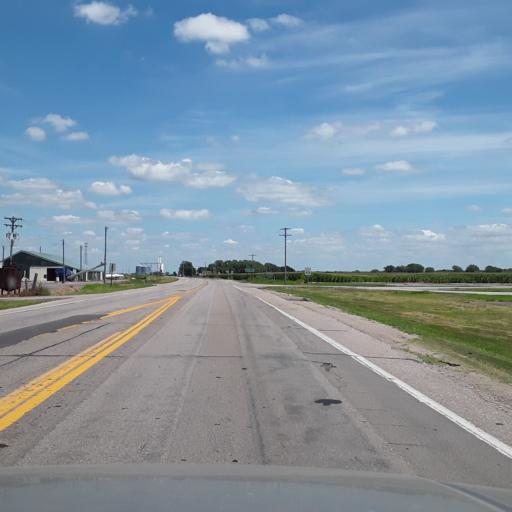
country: US
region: Nebraska
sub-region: Nance County
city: Genoa
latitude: 41.3166
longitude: -97.6610
